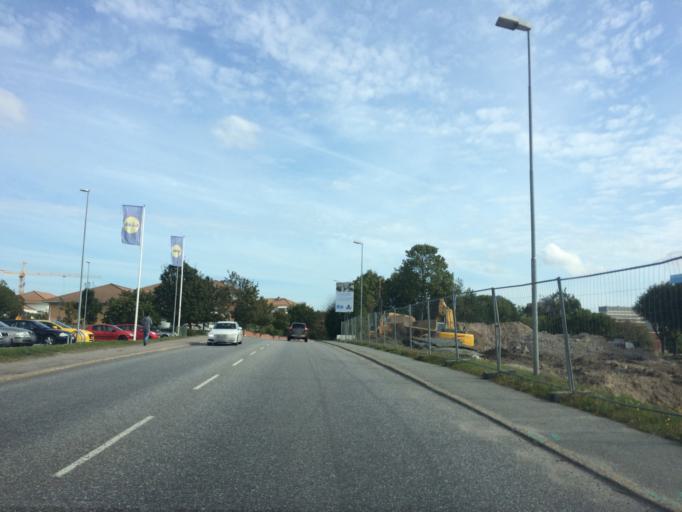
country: SE
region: Stockholm
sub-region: Sollentuna Kommun
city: Sollentuna
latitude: 59.4297
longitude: 17.9363
